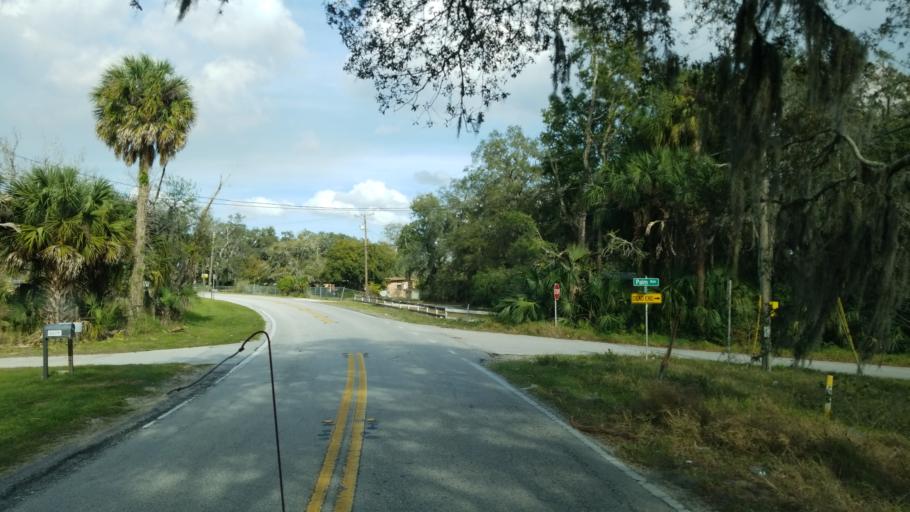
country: US
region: Florida
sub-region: Polk County
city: Loughman
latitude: 28.2364
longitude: -81.5697
